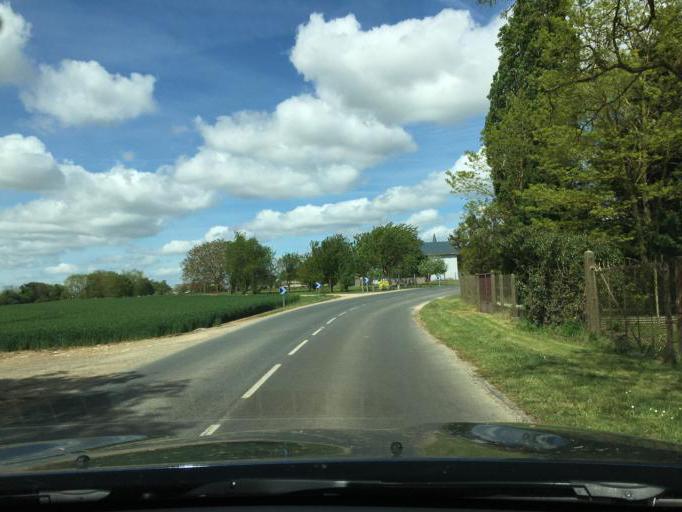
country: FR
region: Centre
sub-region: Departement du Loiret
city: Bricy
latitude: 48.0509
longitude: 1.7921
